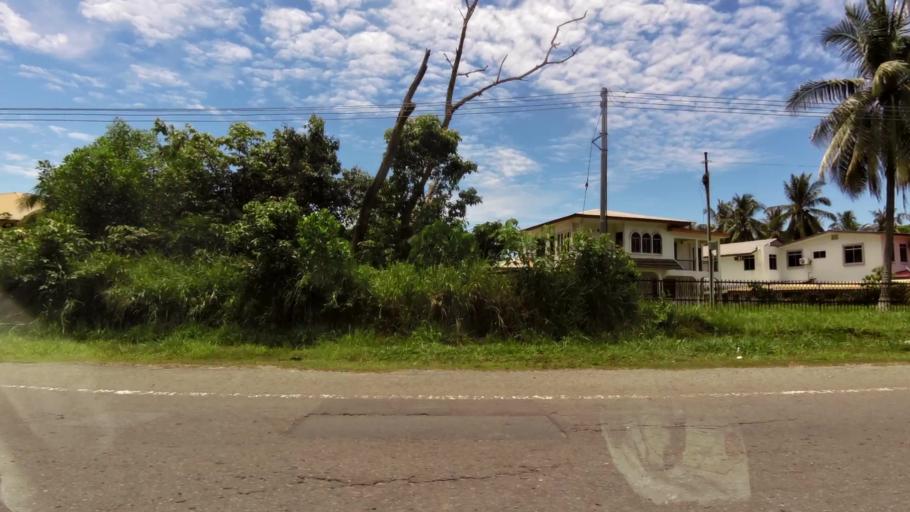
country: BN
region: Brunei and Muara
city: Bandar Seri Begawan
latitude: 4.9995
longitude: 115.0252
